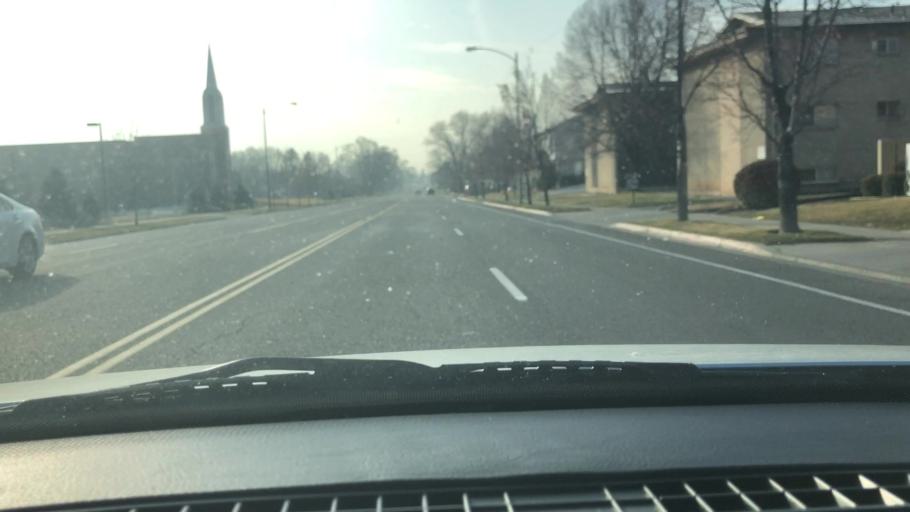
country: US
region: Utah
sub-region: Utah County
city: Provo
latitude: 40.2395
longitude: -111.6432
